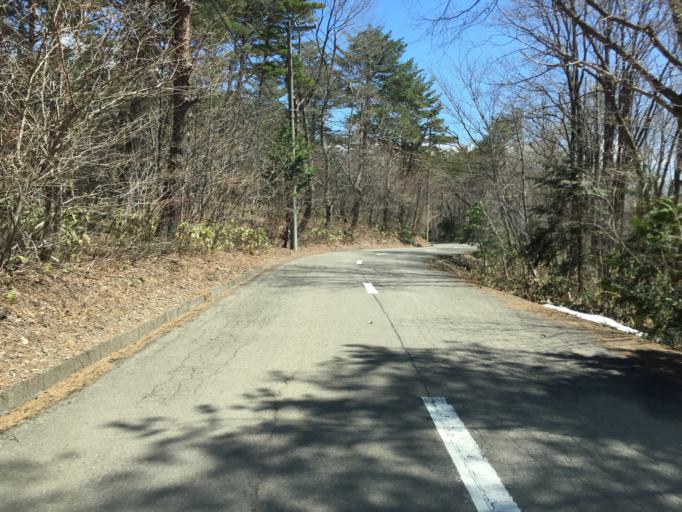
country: JP
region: Fukushima
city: Fukushima-shi
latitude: 37.7534
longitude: 140.3200
